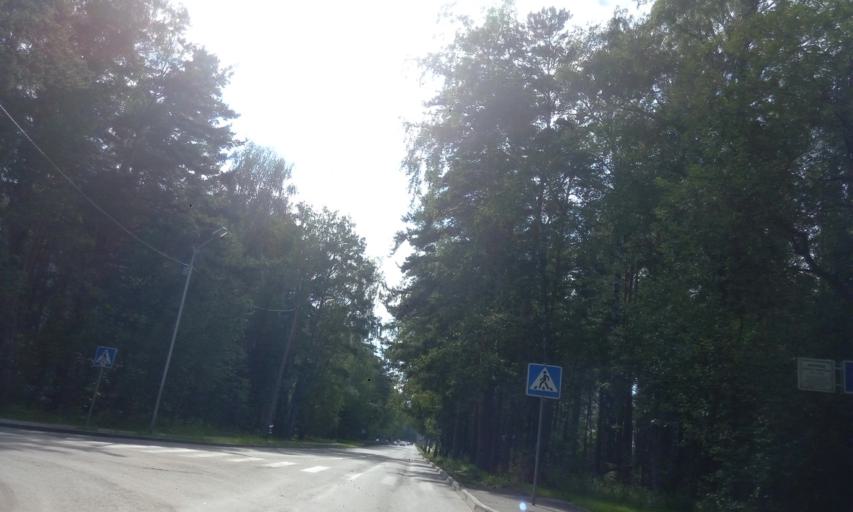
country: RU
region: Novosibirsk
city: Akademgorodok
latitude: 54.8433
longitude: 83.0965
